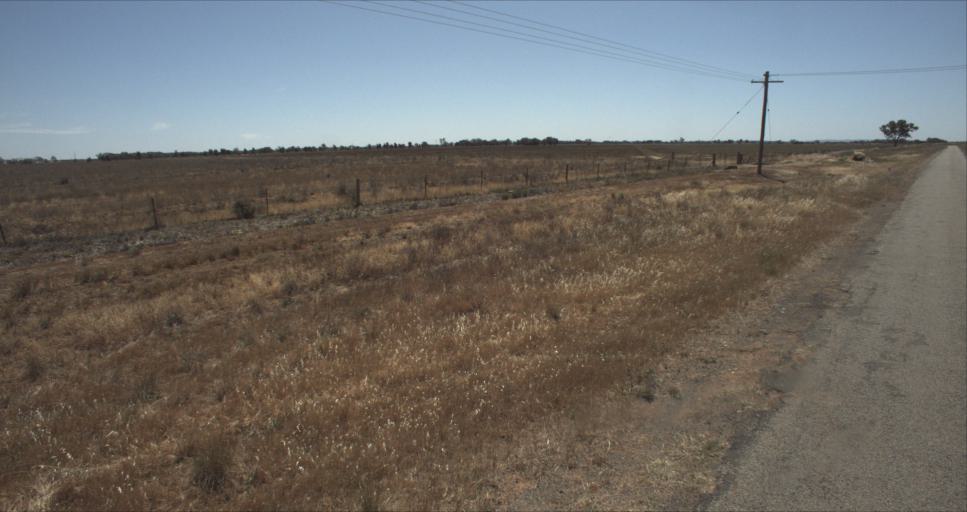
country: AU
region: New South Wales
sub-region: Leeton
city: Leeton
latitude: -34.5052
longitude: 146.3444
